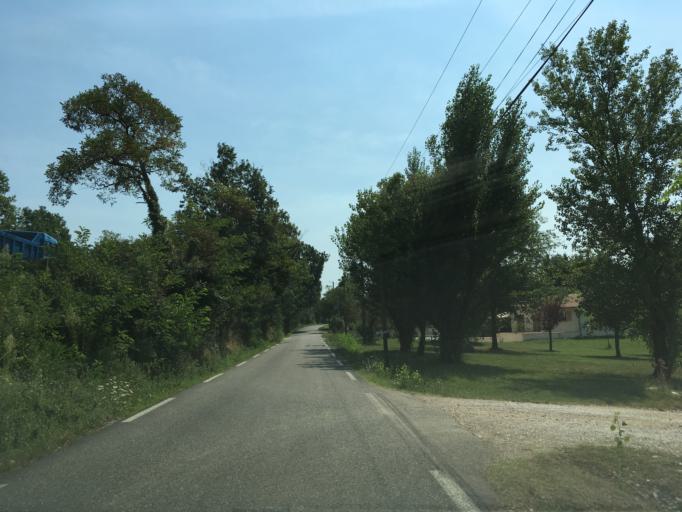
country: FR
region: Midi-Pyrenees
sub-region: Departement du Tarn-et-Garonne
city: Saint-Nauphary
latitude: 43.9733
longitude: 1.3949
